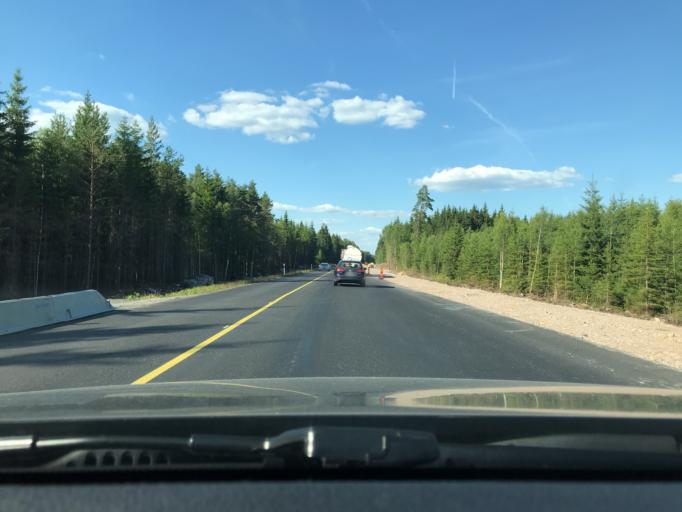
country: SE
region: Kronoberg
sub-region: Almhults Kommun
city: AElmhult
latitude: 56.6317
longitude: 14.2576
